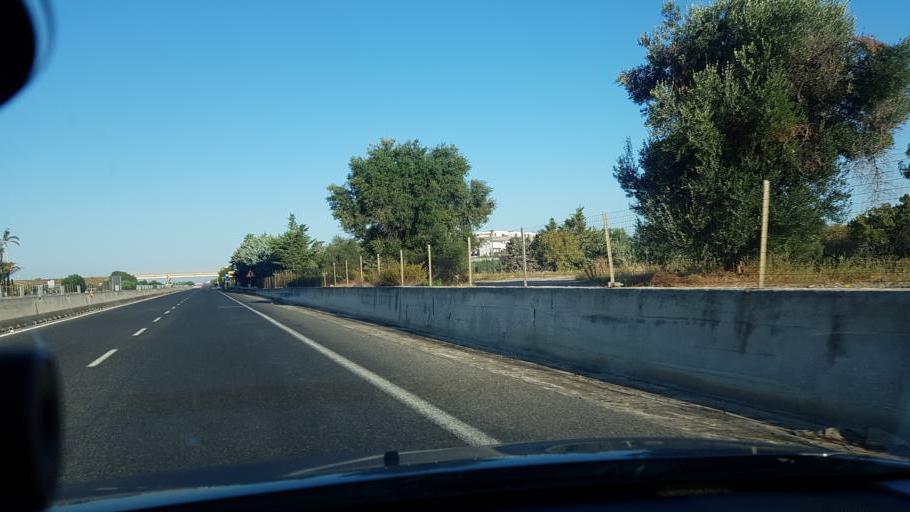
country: IT
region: Apulia
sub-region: Provincia di Bari
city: Monopoli
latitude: 40.9289
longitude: 17.3054
